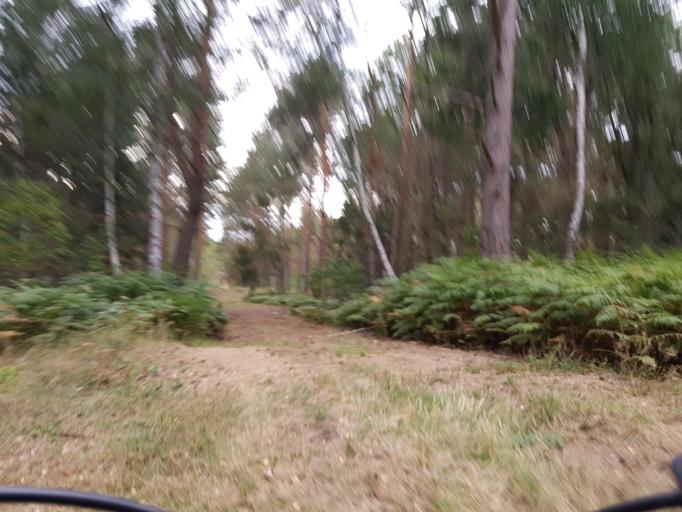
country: DE
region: Brandenburg
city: Trobitz
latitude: 51.5545
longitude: 13.4516
